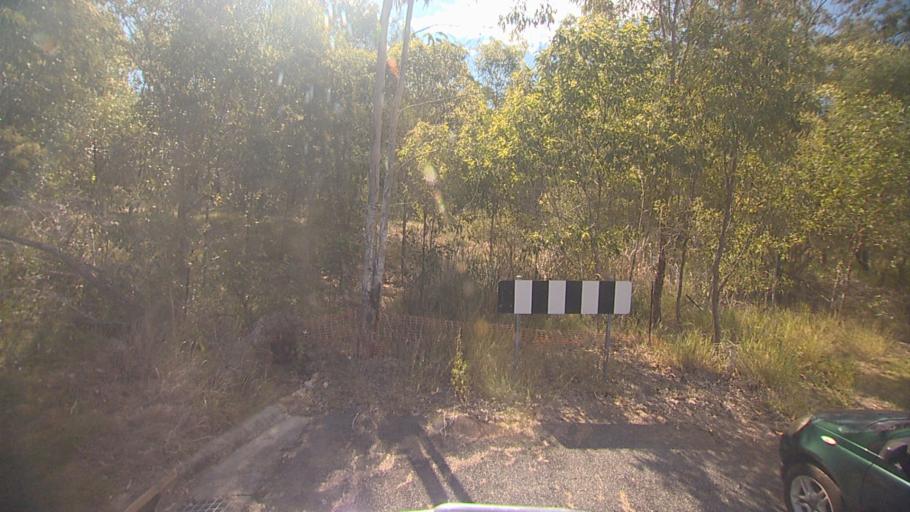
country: AU
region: Queensland
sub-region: Ipswich
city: Springfield Lakes
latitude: -27.7471
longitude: 152.9374
